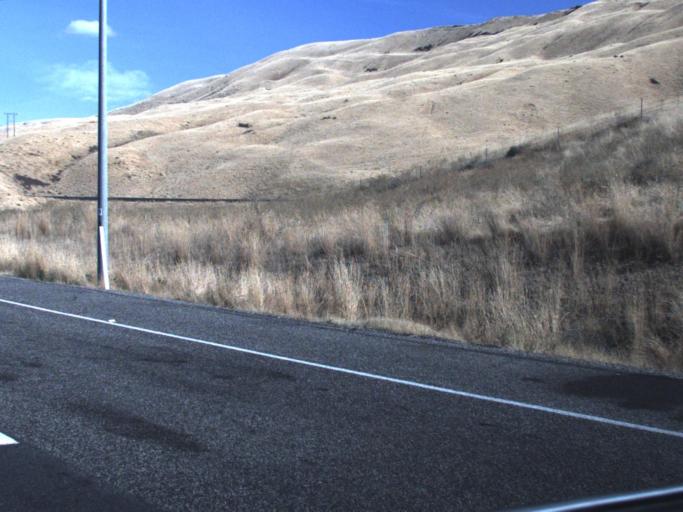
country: US
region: Washington
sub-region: Benton County
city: Benton City
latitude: 46.2468
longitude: -119.6248
